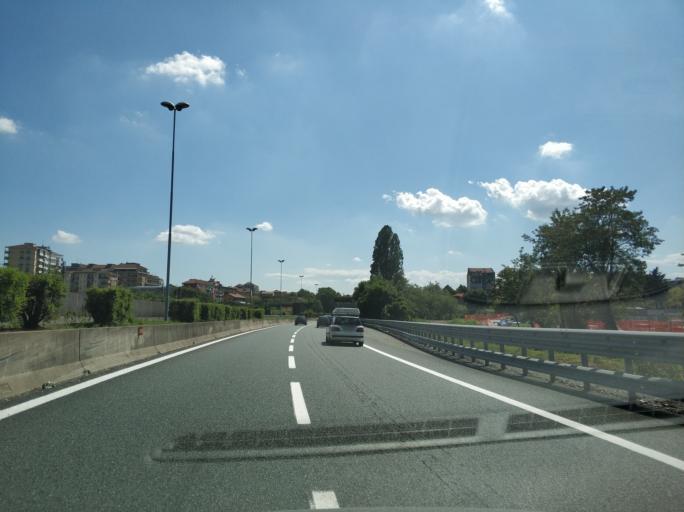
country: IT
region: Piedmont
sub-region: Provincia di Torino
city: Turin
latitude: 45.1097
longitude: 7.6956
